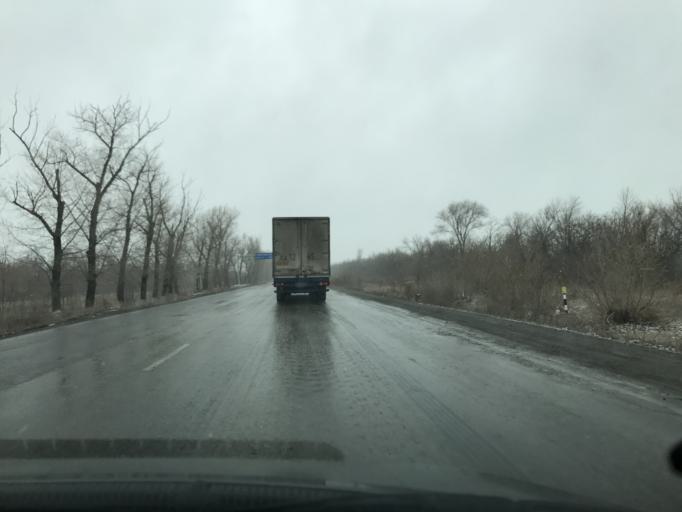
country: RU
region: Rostov
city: Bataysk
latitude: 47.0793
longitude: 39.7776
